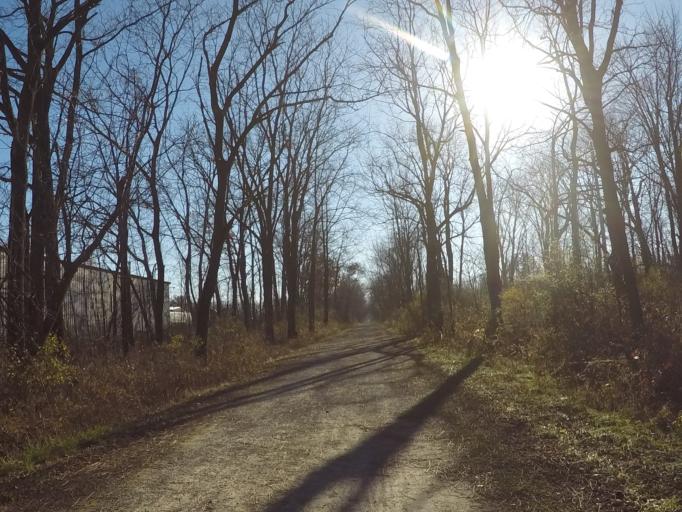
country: US
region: Wisconsin
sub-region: Dane County
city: Deerfield
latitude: 43.0529
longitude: -89.0679
